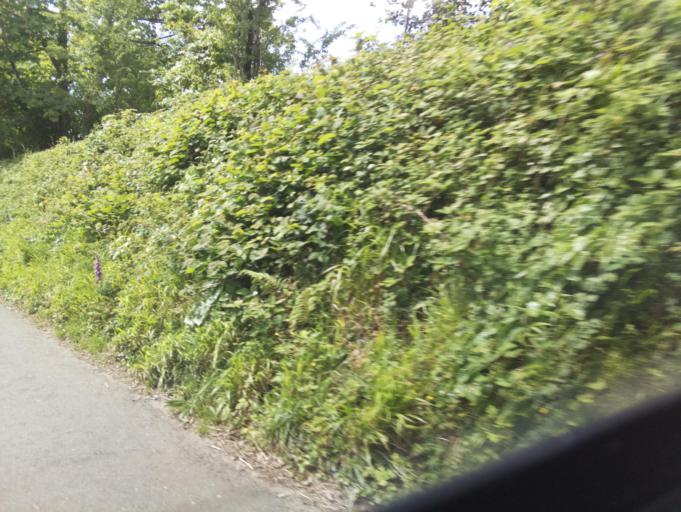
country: GB
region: England
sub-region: Devon
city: Kingsbridge
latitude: 50.3647
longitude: -3.7728
